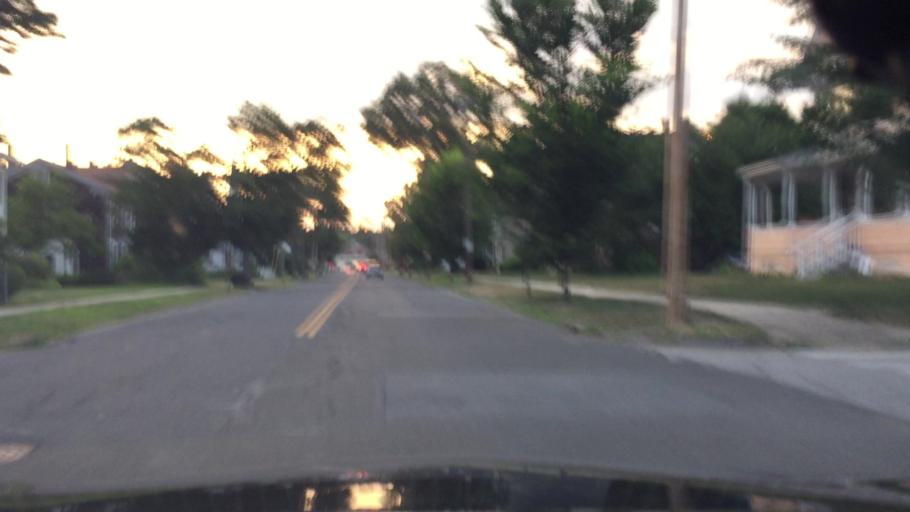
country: US
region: Connecticut
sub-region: Fairfield County
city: Stratford
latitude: 41.1928
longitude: -73.1272
